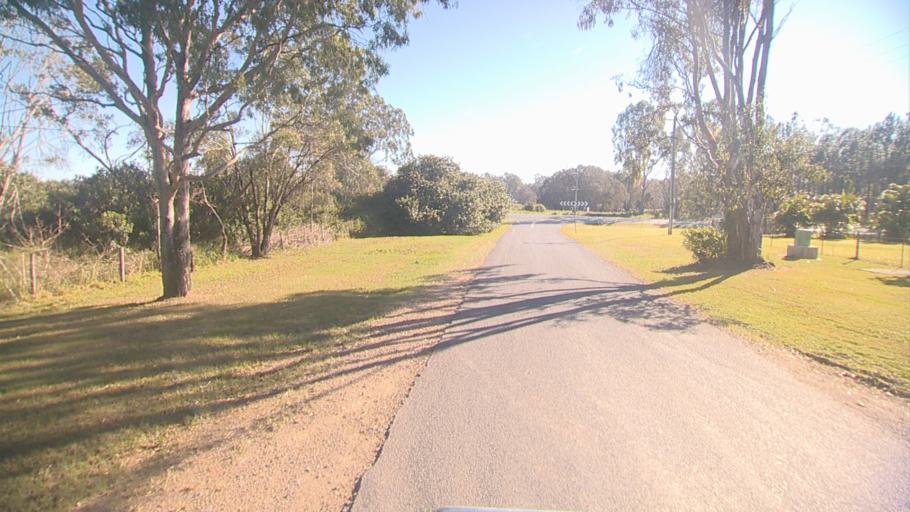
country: AU
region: Queensland
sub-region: Gold Coast
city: Yatala
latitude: -27.6855
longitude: 153.2601
